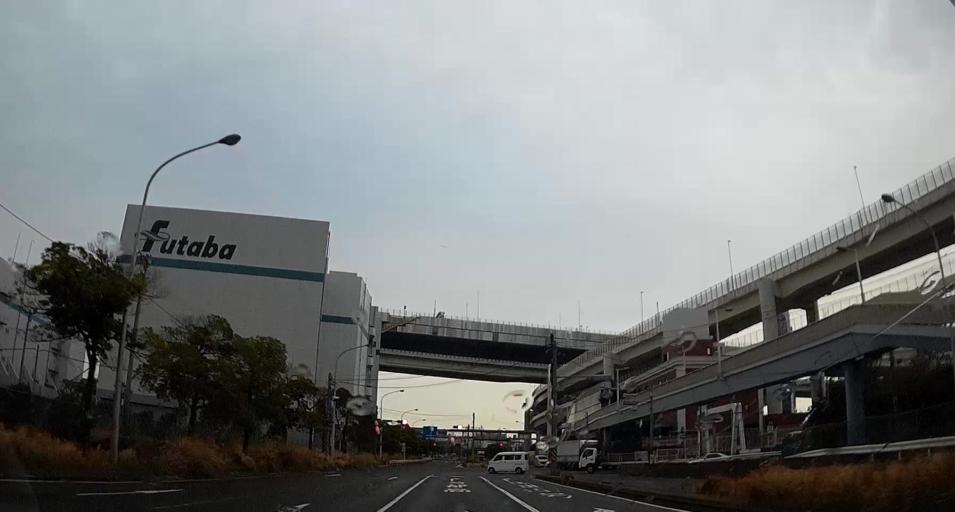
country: JP
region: Kanagawa
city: Yokohama
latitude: 35.4601
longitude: 139.6802
